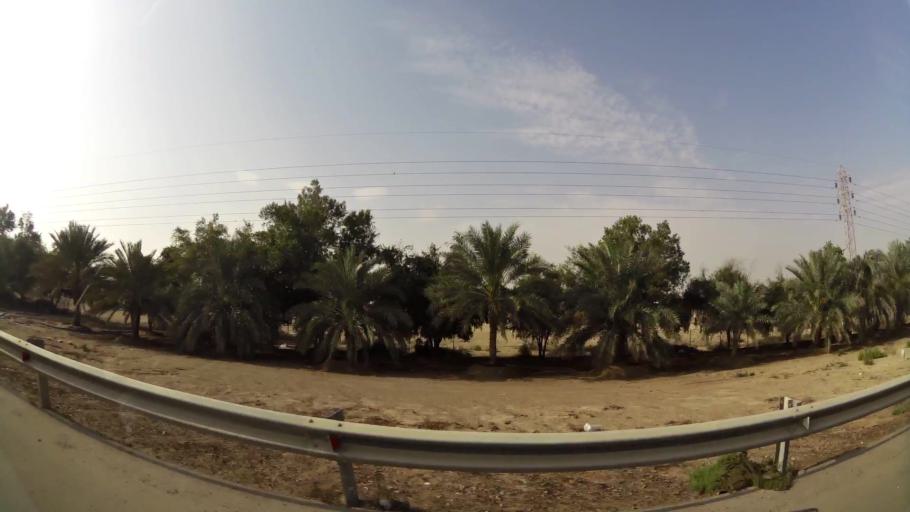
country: AE
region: Abu Dhabi
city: Abu Dhabi
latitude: 24.2699
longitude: 54.6637
